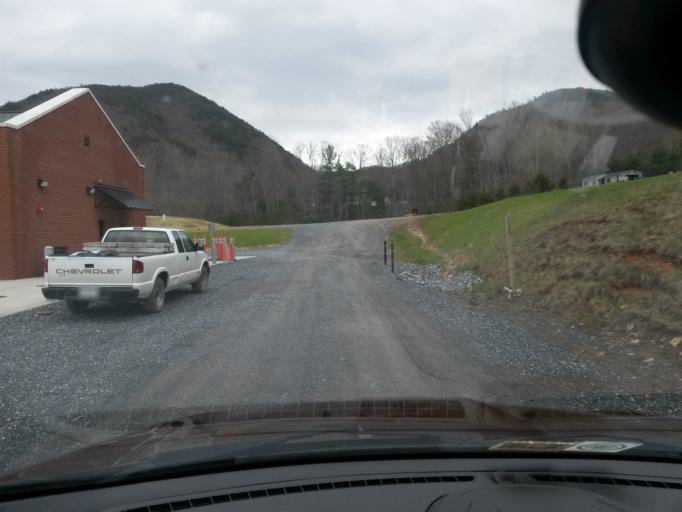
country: US
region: Virginia
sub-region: City of Buena Vista
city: Buena Vista
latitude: 37.7415
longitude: -79.3388
